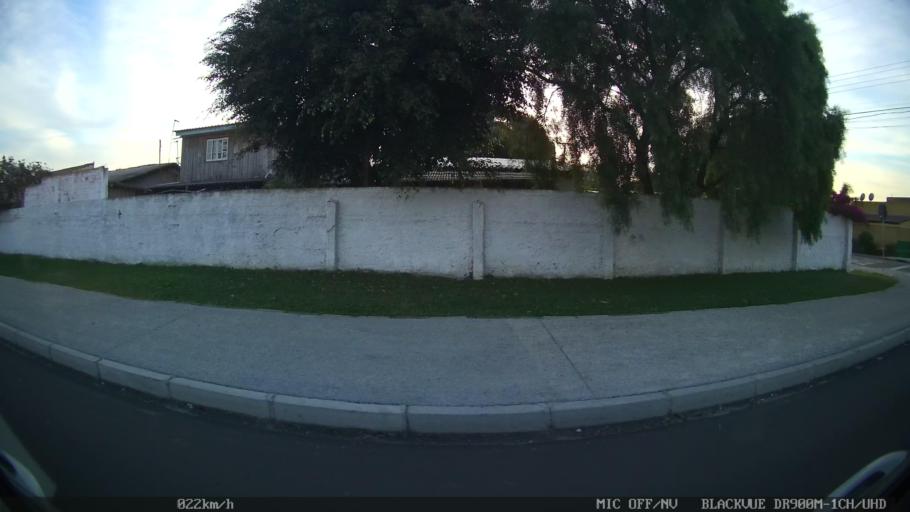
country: BR
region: Parana
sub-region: Pinhais
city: Pinhais
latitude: -25.4621
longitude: -49.1862
